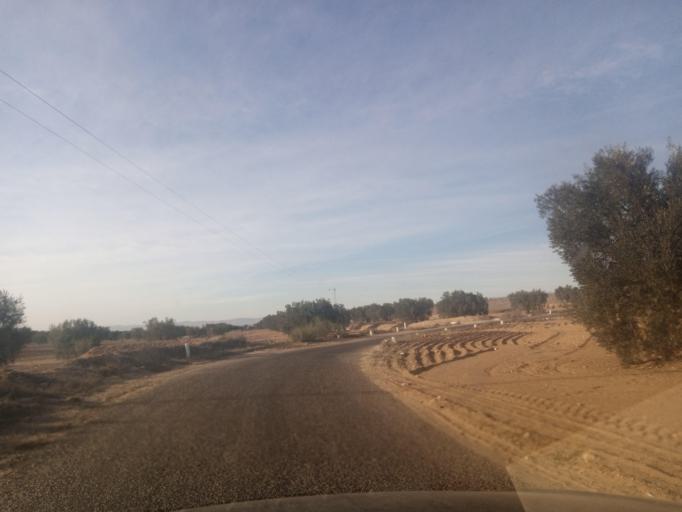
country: TN
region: Safaqis
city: Bi'r `Ali Bin Khalifah
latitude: 34.8450
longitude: 10.1598
